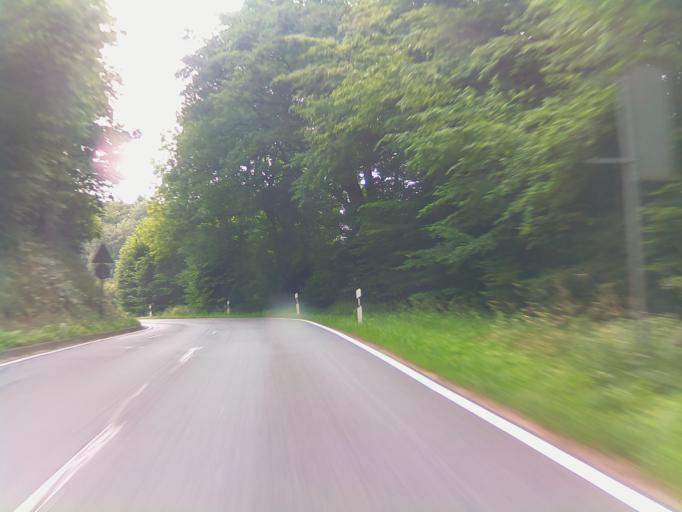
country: DE
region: Hesse
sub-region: Regierungsbezirk Darmstadt
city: Furth
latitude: 49.6598
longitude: 8.7711
